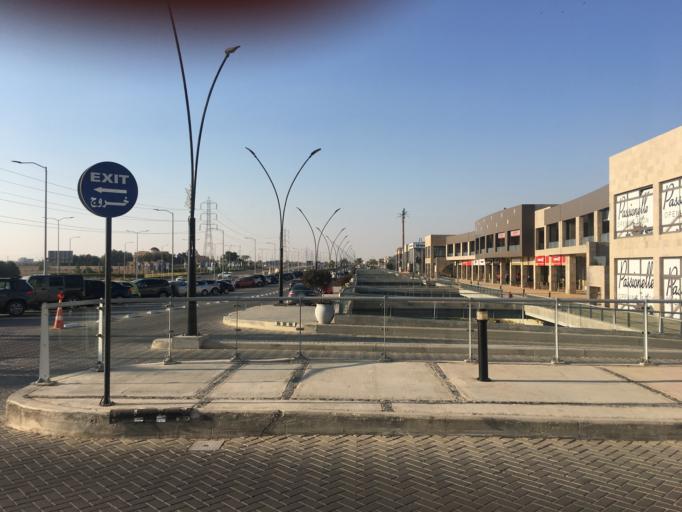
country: EG
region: Al Jizah
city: Awsim
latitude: 30.0555
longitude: 30.9424
